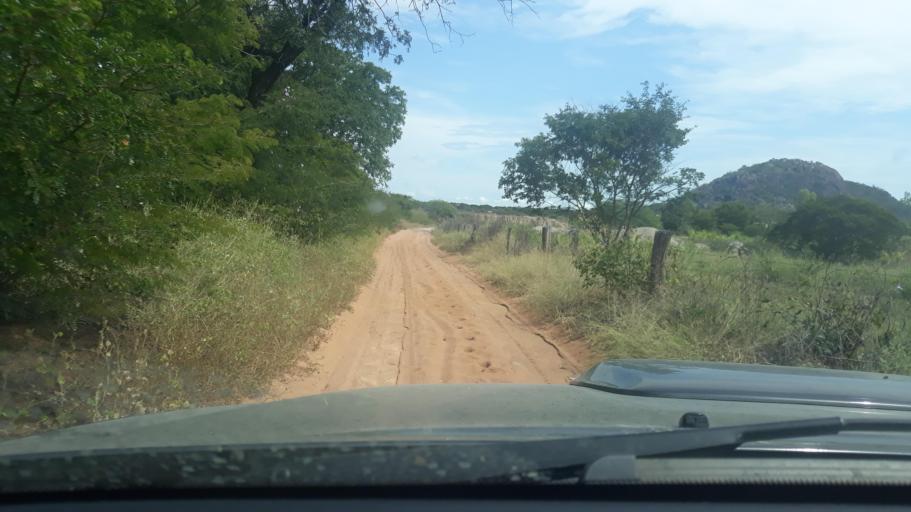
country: BR
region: Bahia
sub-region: Riacho De Santana
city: Riacho de Santana
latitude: -13.8566
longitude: -43.0454
